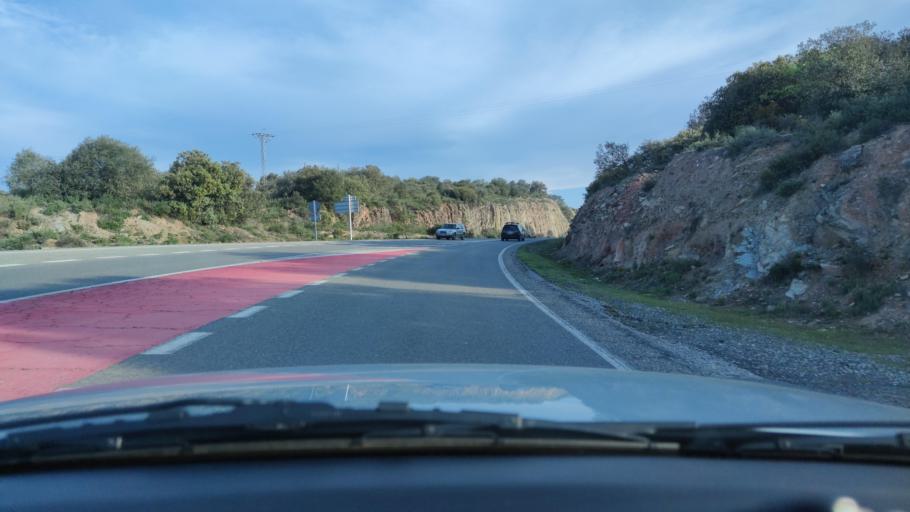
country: ES
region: Catalonia
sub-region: Provincia de Lleida
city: Artesa de Segre
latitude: 41.8475
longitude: 1.0575
